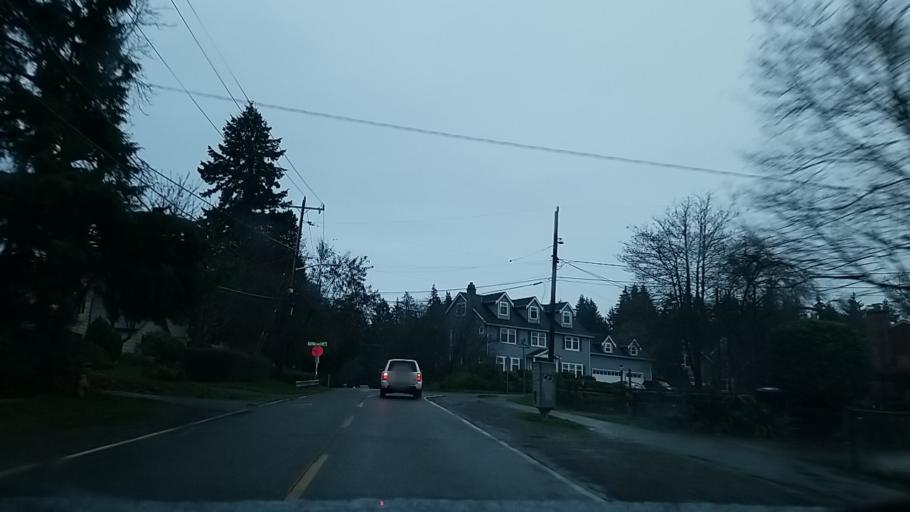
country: US
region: Washington
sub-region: King County
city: Shoreline
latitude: 47.7220
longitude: -122.3316
